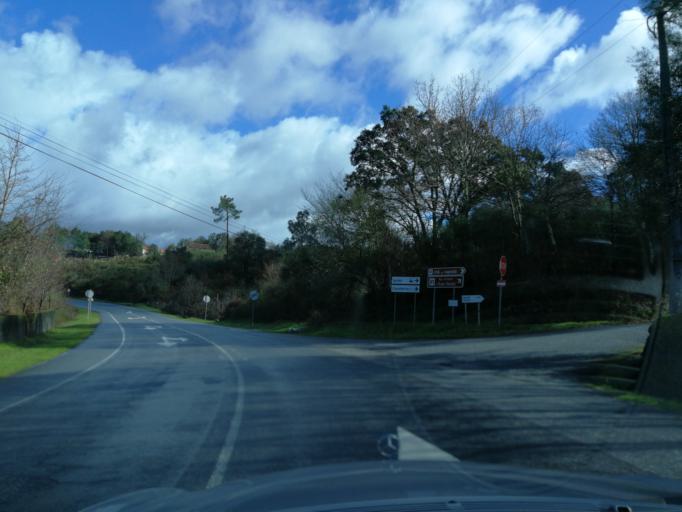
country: PT
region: Braga
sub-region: Terras de Bouro
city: Antas
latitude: 41.8319
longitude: -8.3000
